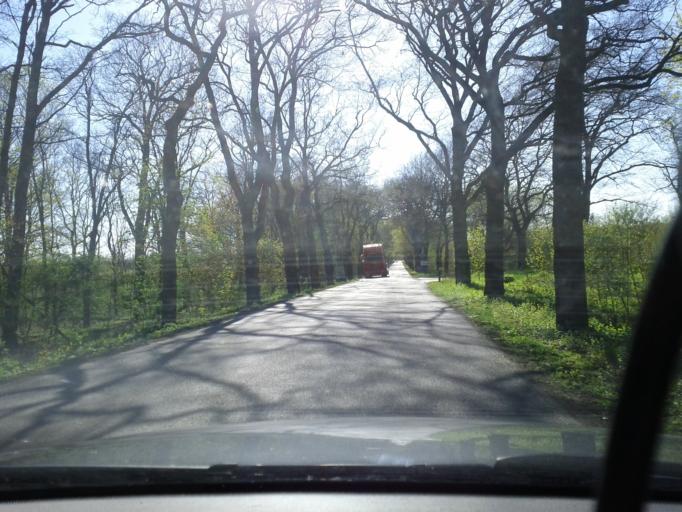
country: DE
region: Brandenburg
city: Hoppegarten
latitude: 52.4860
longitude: 13.6548
